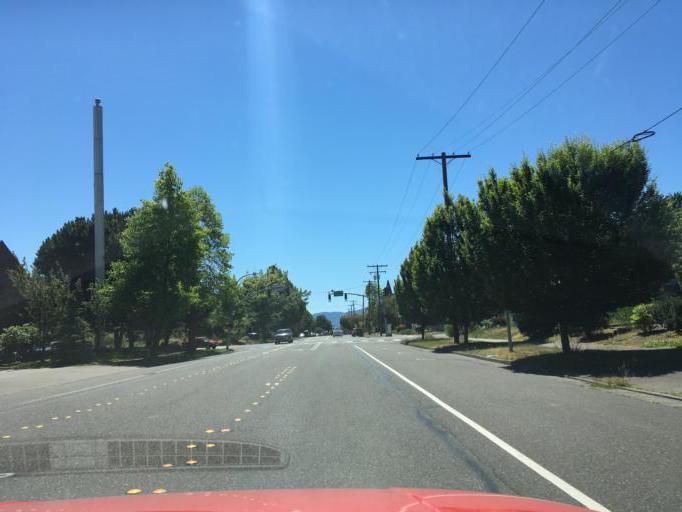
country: US
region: Washington
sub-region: Whatcom County
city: Bellingham
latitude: 48.7604
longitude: -122.4876
